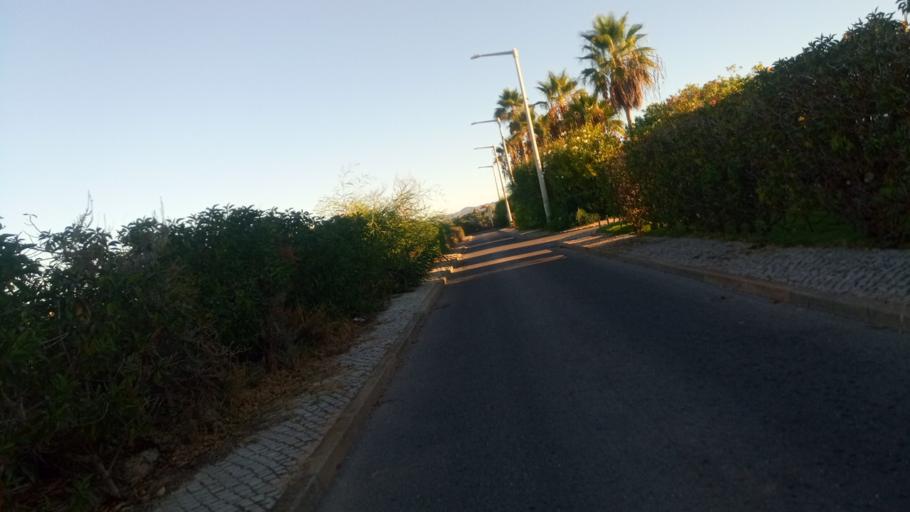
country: PT
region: Faro
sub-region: Tavira
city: Tavira
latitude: 37.1313
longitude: -7.6104
